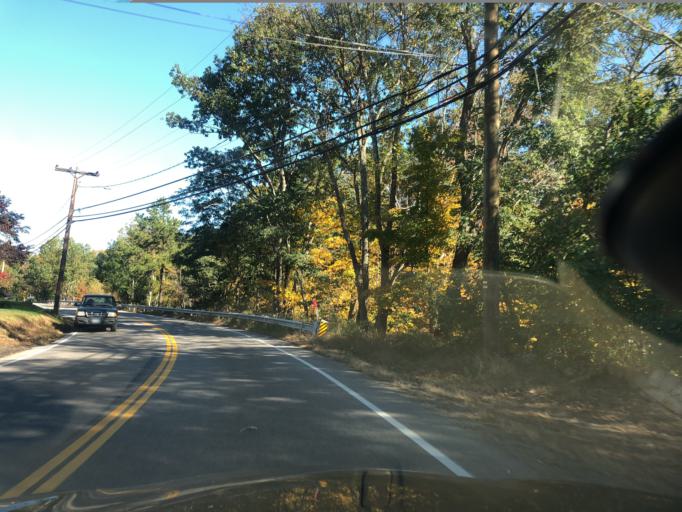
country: US
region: New Hampshire
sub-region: Rockingham County
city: Newmarket
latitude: 43.0633
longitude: -70.9364
